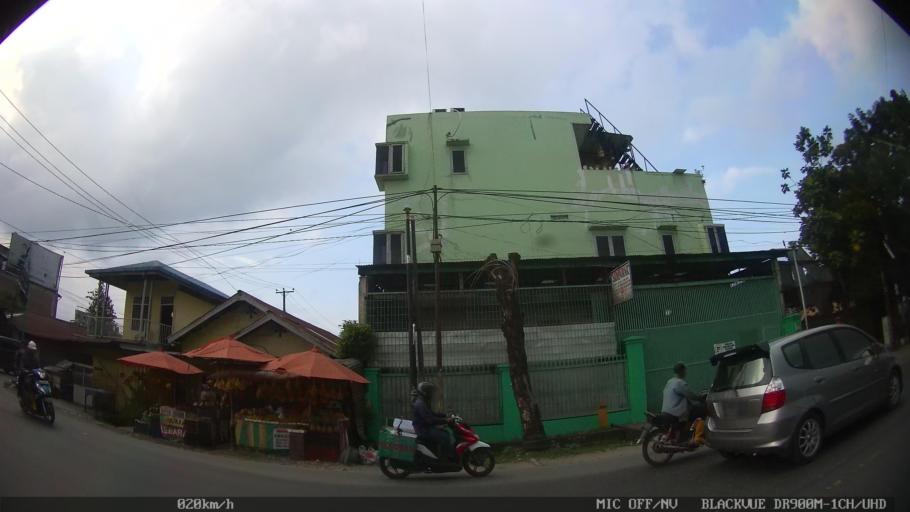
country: ID
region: North Sumatra
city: Medan
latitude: 3.5971
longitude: 98.7294
